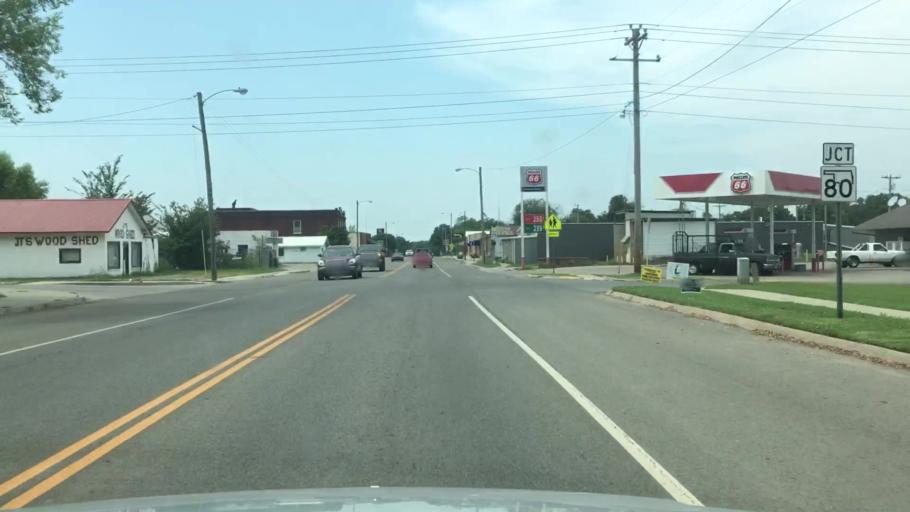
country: US
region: Oklahoma
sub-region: Cherokee County
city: Tahlequah
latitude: 35.9328
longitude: -95.1410
